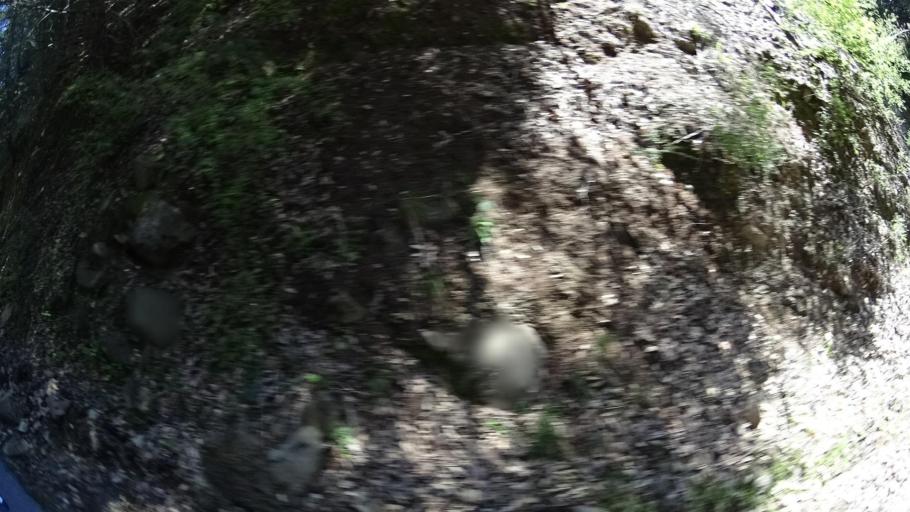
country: US
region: California
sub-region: Humboldt County
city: Rio Dell
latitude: 40.3024
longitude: -124.0568
